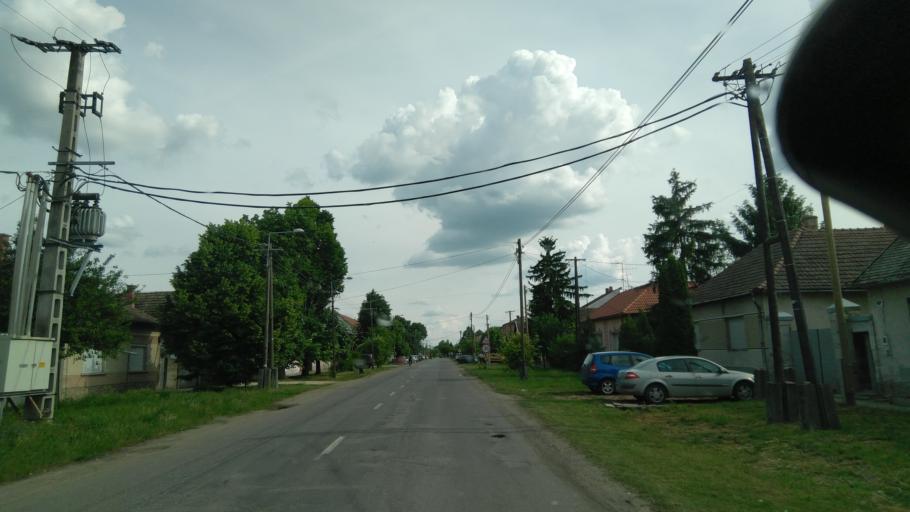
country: HU
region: Bekes
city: Battonya
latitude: 46.2889
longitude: 21.0172
